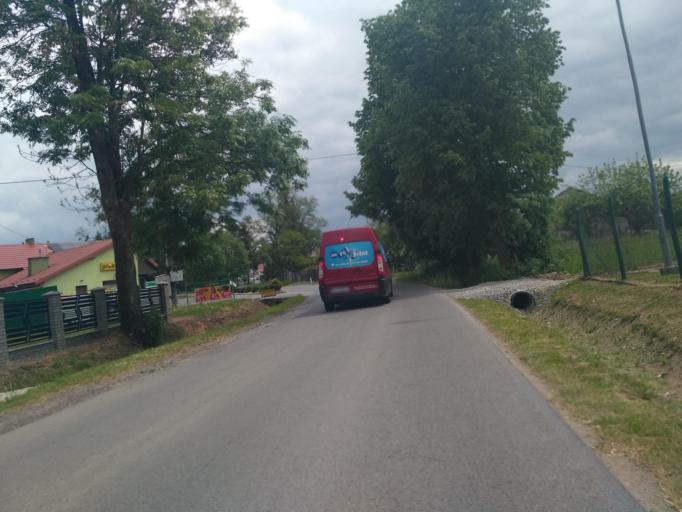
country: PL
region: Subcarpathian Voivodeship
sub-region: Powiat krosnienski
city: Jedlicze
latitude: 49.7054
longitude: 21.6378
